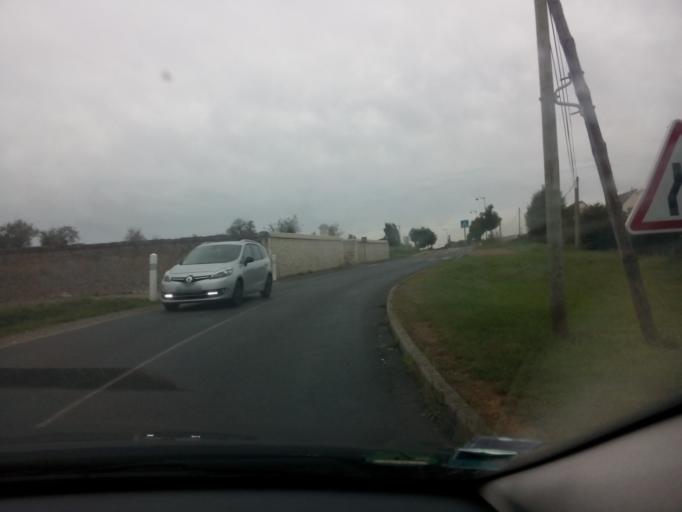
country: FR
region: Pays de la Loire
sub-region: Departement de Maine-et-Loire
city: Baune
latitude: 47.5006
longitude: -0.3231
